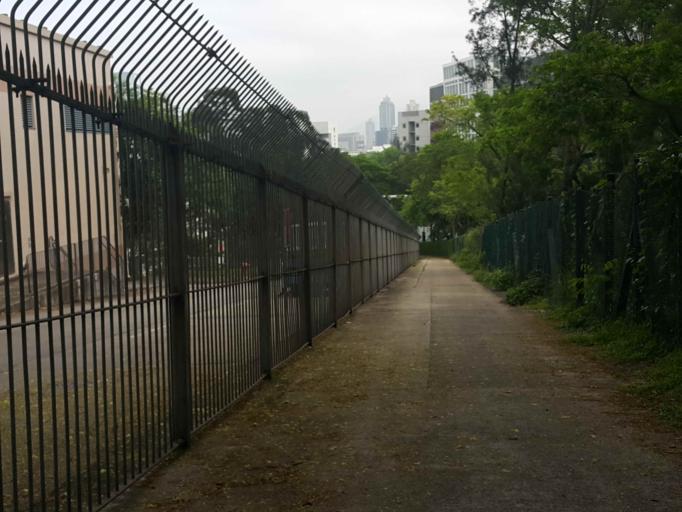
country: HK
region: Wong Tai Sin
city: Wong Tai Sin
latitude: 22.3392
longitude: 114.1741
